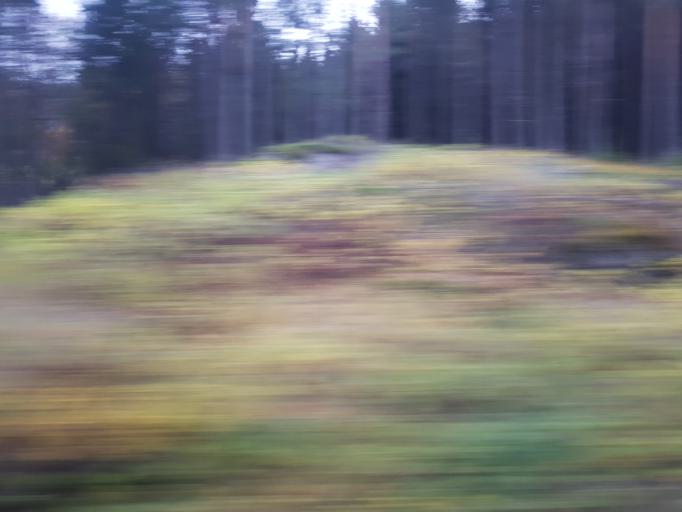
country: NO
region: Oppland
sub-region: Dovre
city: Dovre
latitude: 61.9270
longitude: 9.3250
